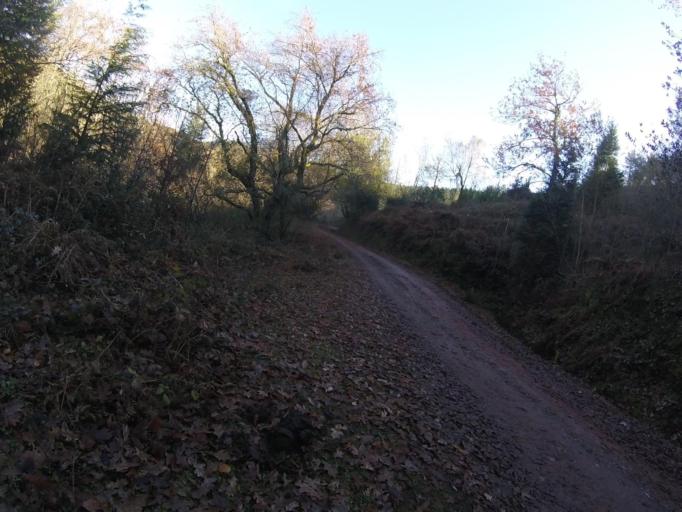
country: ES
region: Navarre
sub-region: Provincia de Navarra
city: Bera
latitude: 43.3188
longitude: -1.7058
